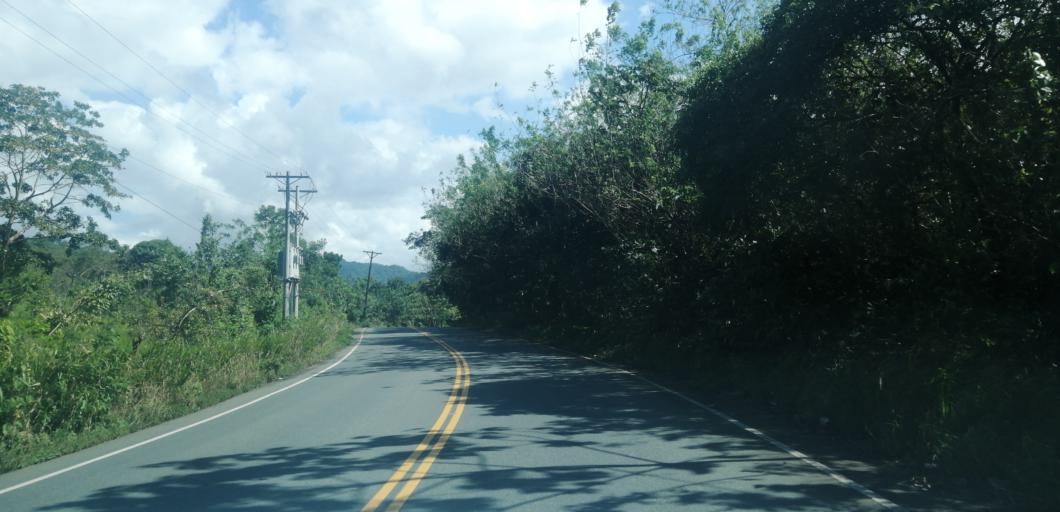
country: PA
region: Panama
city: Canita
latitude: 9.2204
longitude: -78.9256
